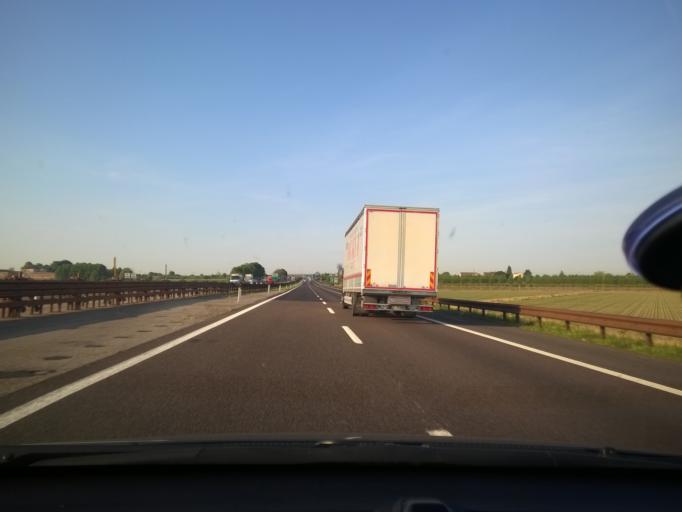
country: IT
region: Lombardy
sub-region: Provincia di Mantova
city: San Biagio
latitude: 45.1000
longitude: 10.8586
